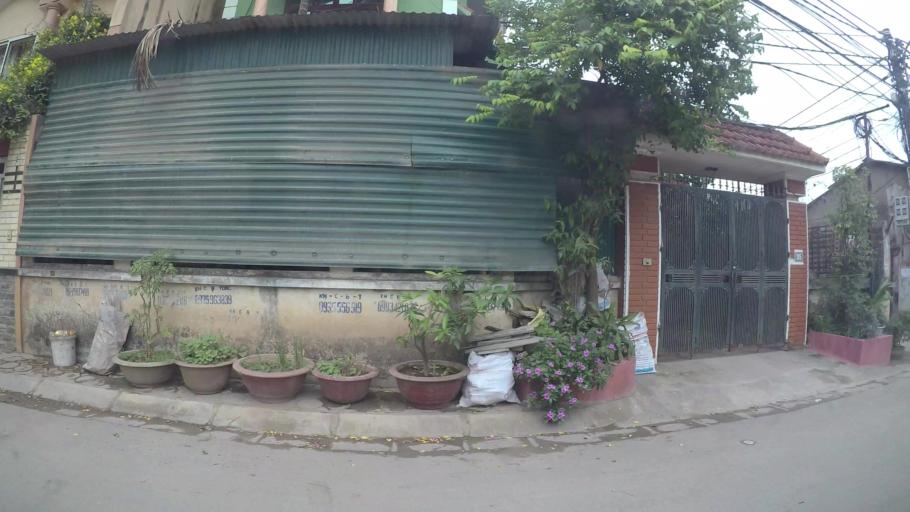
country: VN
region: Ha Noi
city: Tay Ho
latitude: 21.0886
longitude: 105.7919
